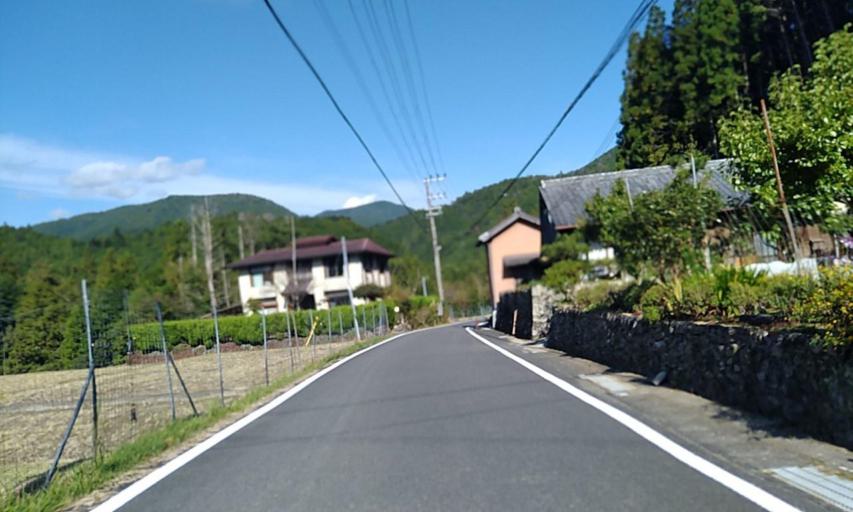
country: JP
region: Wakayama
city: Shingu
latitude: 33.9281
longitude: 135.9798
